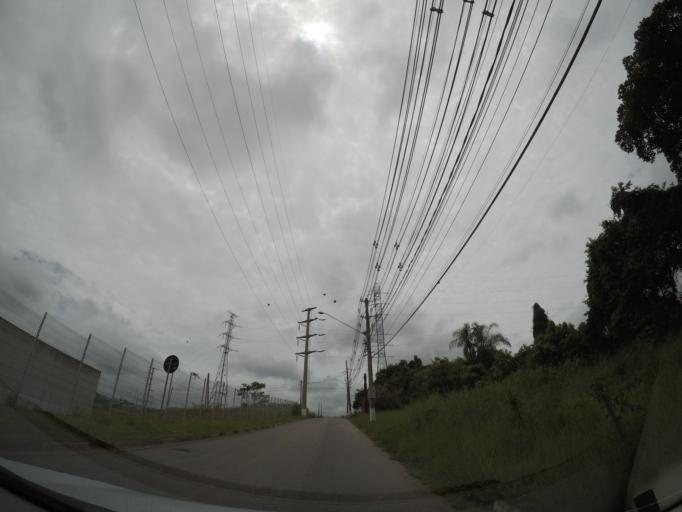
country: BR
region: Sao Paulo
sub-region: Louveira
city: Louveira
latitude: -23.0705
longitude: -46.9896
